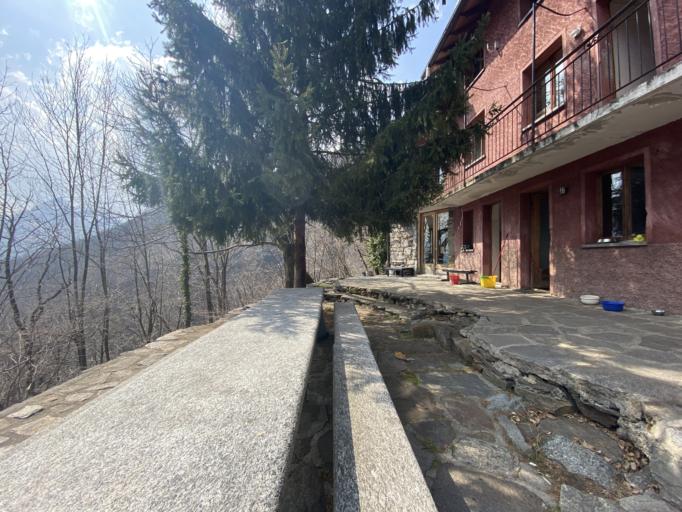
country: IT
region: Piedmont
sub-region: Provincia Verbano-Cusio-Ossola
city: Cursolo
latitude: 46.1060
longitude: 8.5943
